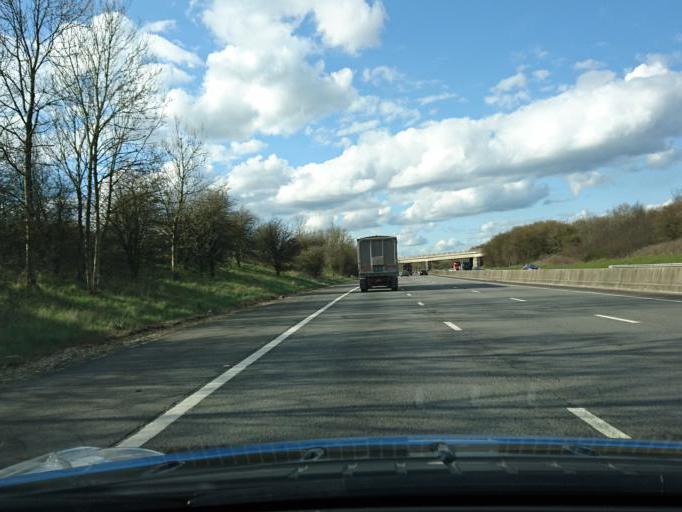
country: GB
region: England
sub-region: Wiltshire
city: Aldbourne
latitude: 51.4937
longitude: -1.5815
